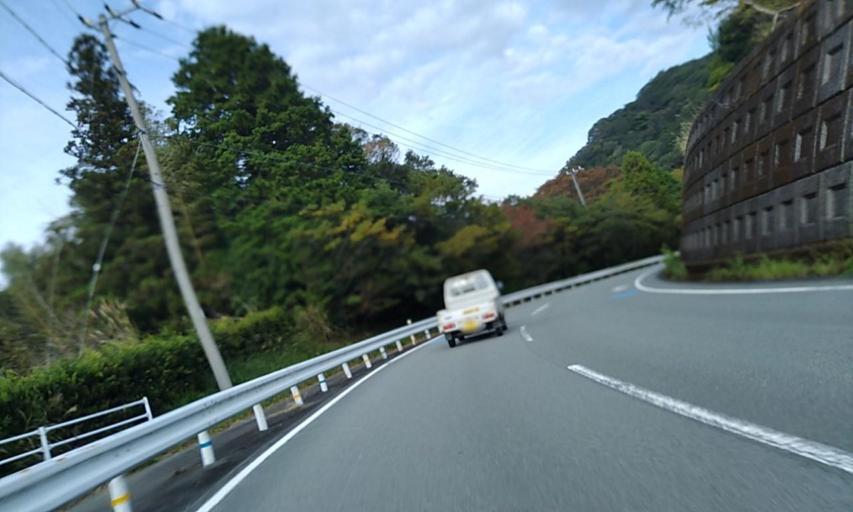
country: JP
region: Mie
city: Ise
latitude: 34.2982
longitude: 136.6024
